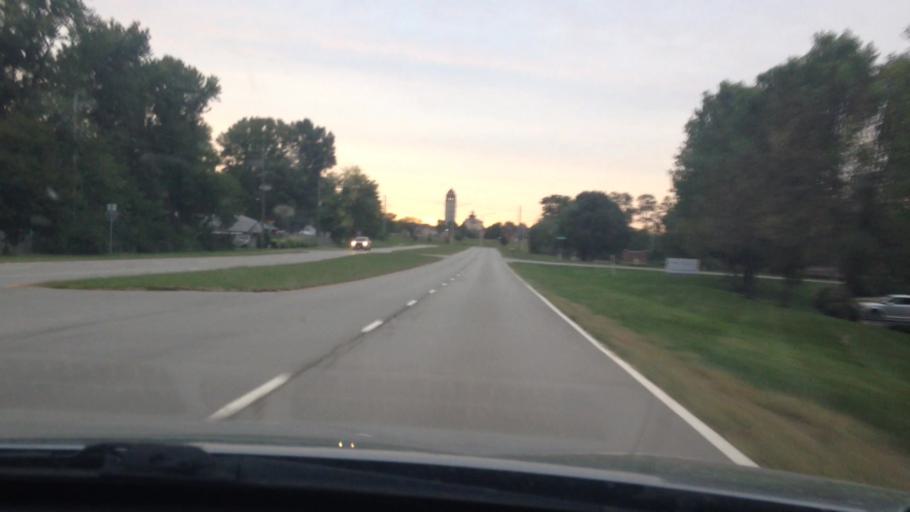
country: US
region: Missouri
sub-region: Jackson County
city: Lees Summit
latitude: 38.9382
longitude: -94.4041
